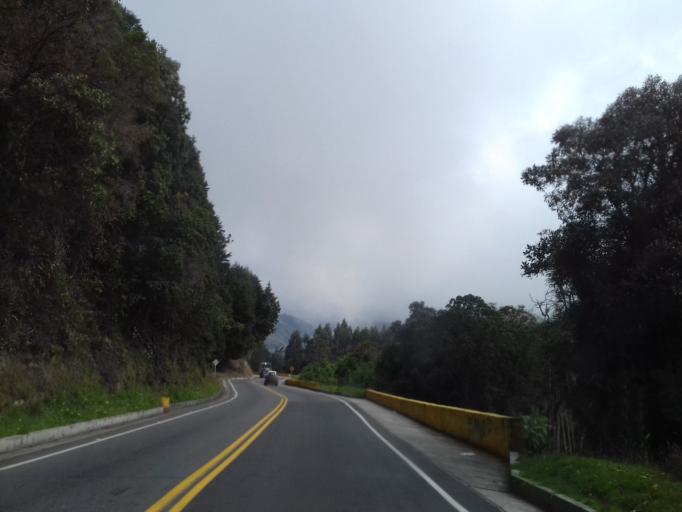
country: CO
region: Caldas
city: Villamaria
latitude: 5.0167
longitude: -75.3628
